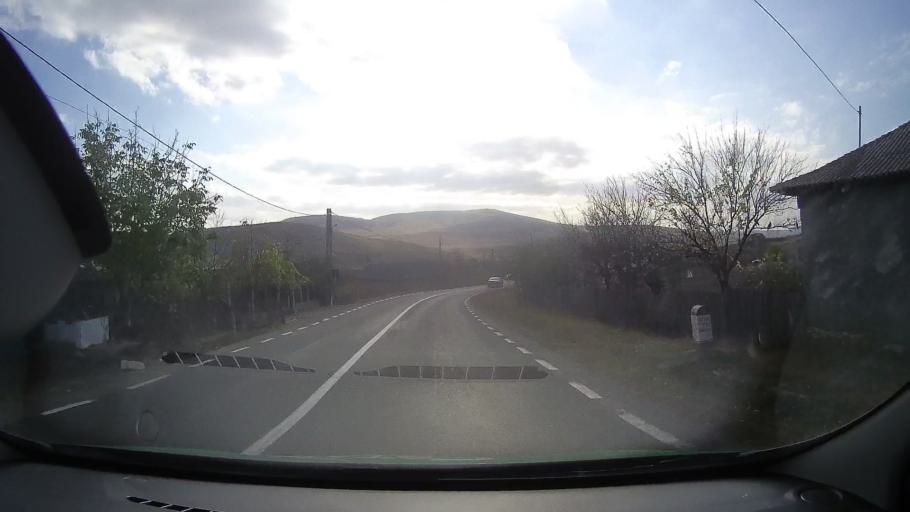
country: RO
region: Tulcea
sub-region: Comuna Nalbant
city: Nicolae Balcescu
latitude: 44.9968
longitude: 28.5887
